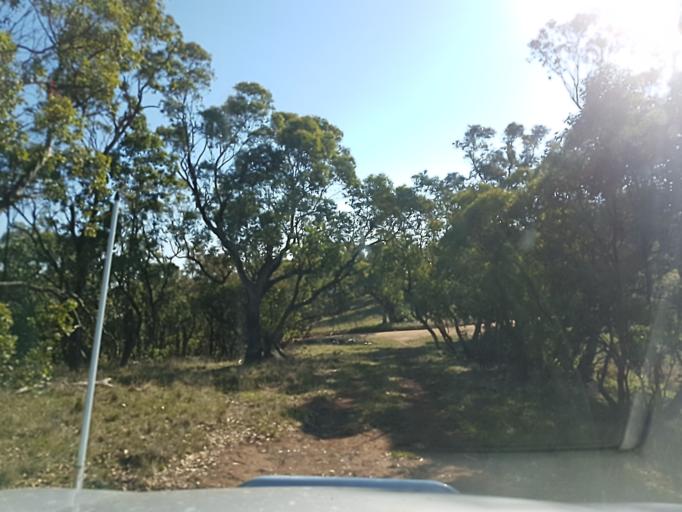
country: AU
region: New South Wales
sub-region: Snowy River
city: Jindabyne
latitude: -36.9507
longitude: 148.3511
